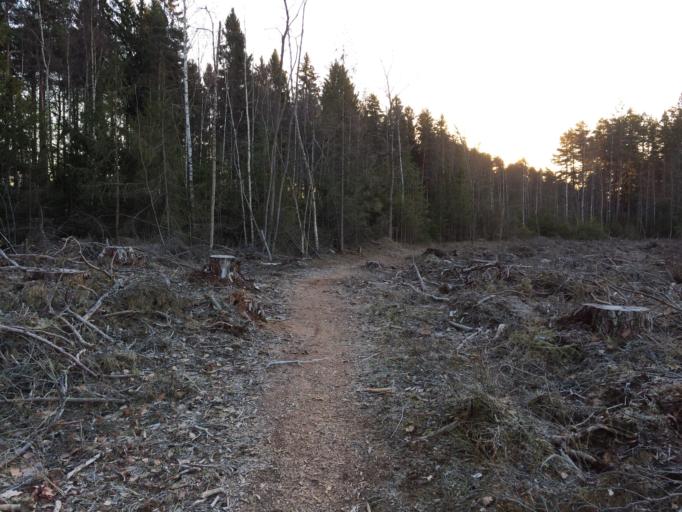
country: SE
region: Vaestmanland
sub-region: Hallstahammars Kommun
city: Hallstahammar
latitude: 59.6198
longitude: 16.1989
